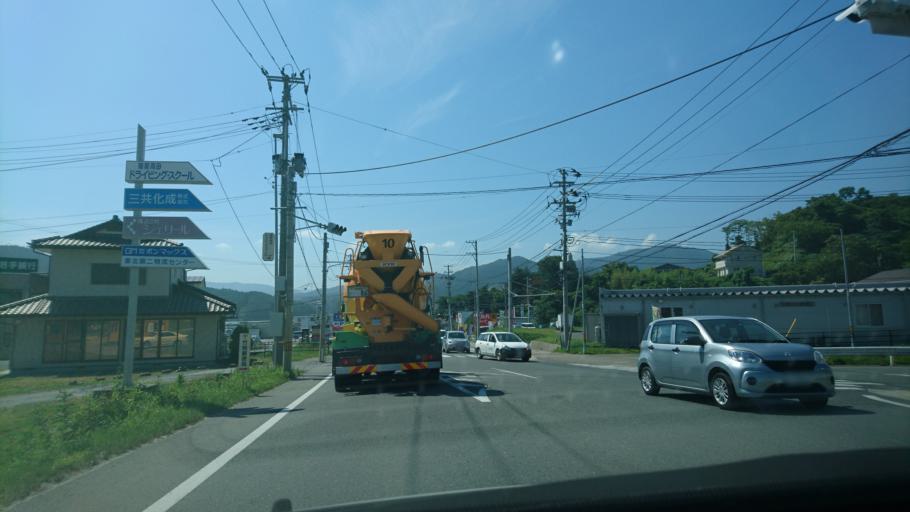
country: JP
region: Iwate
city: Ofunato
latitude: 39.0317
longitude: 141.6196
